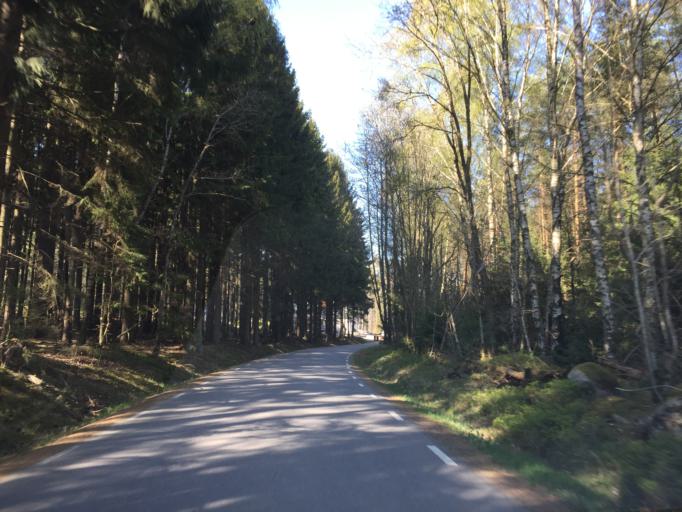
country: SE
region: Vaestra Goetaland
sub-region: Ale Kommun
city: Surte
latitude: 57.8241
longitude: 11.9894
